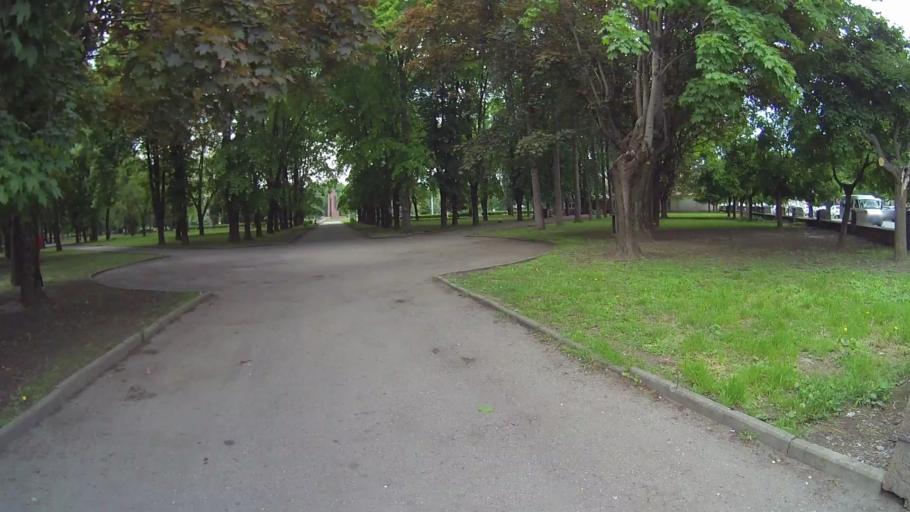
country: RU
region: Kabardino-Balkariya
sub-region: Gorod Nal'chik
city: Nal'chik
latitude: 43.4873
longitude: 43.6085
